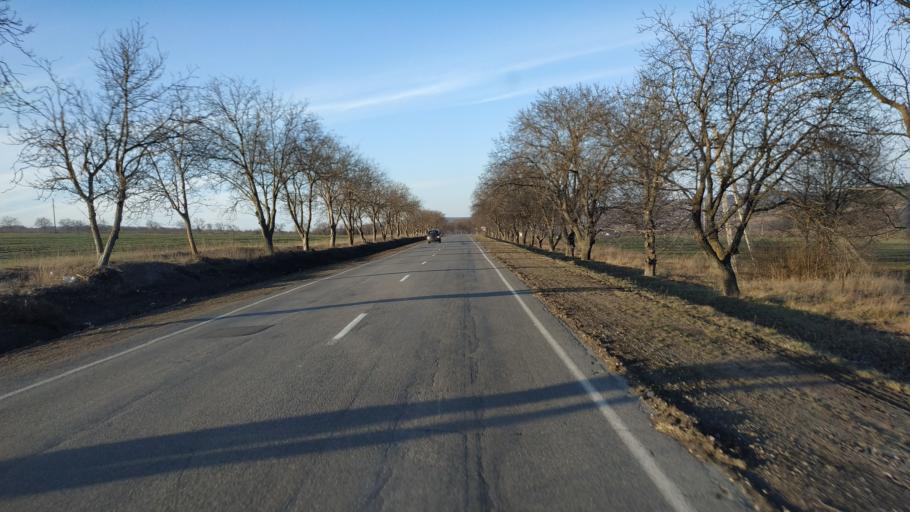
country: MD
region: Hincesti
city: Hincesti
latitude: 46.7775
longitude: 28.5245
